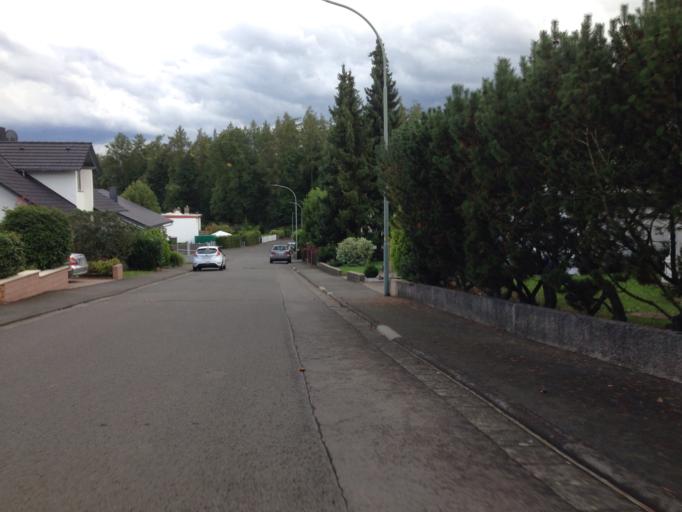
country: DE
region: Hesse
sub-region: Regierungsbezirk Giessen
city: Hungen
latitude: 50.4696
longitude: 8.8924
